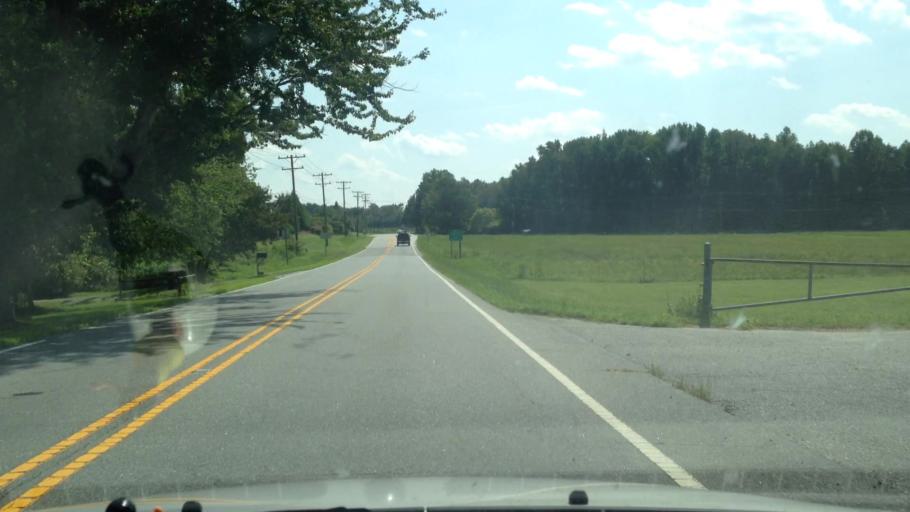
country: US
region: North Carolina
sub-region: Forsyth County
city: Kernersville
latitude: 36.1504
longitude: -80.0379
